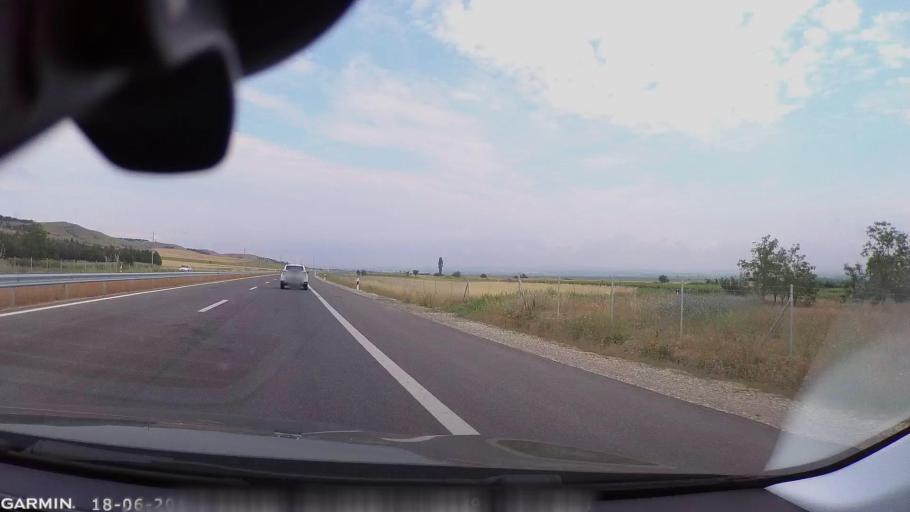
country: MK
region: Stip
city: Shtip
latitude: 41.7978
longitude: 22.0844
